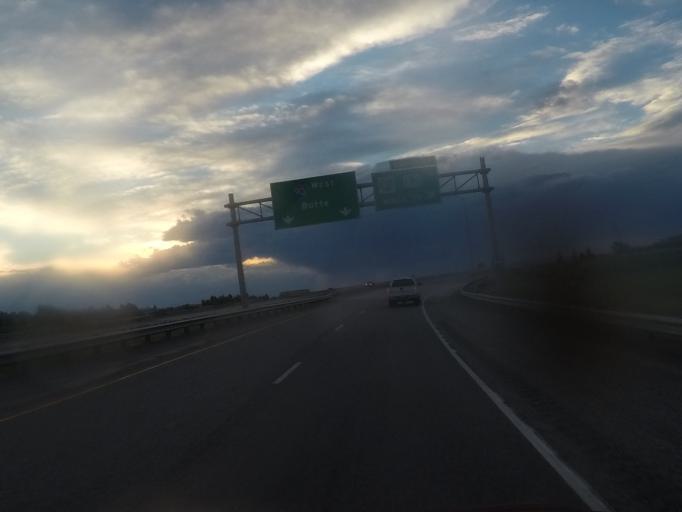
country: US
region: Montana
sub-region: Gallatin County
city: Bozeman
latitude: 45.6746
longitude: -111.0096
